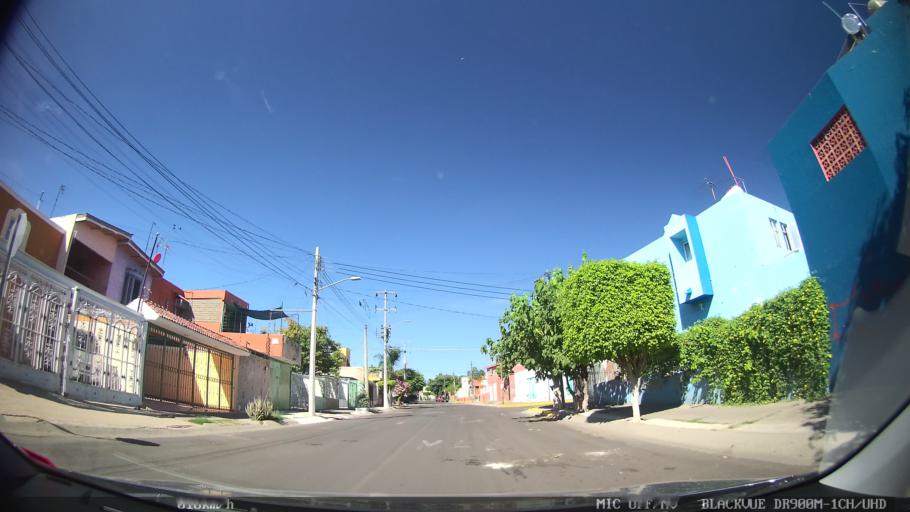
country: MX
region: Jalisco
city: Tlaquepaque
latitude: 20.6804
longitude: -103.2711
